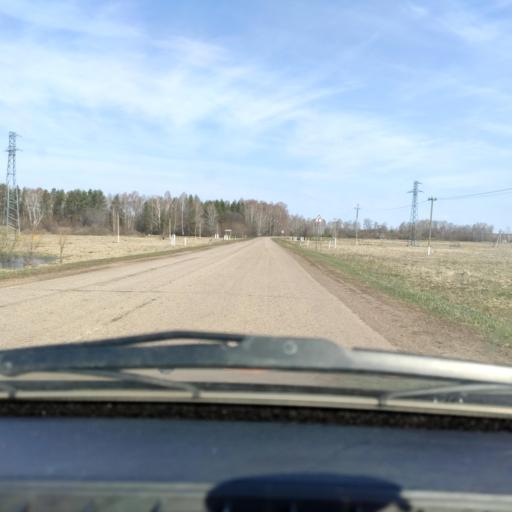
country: RU
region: Bashkortostan
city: Asanovo
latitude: 54.7704
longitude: 55.4879
